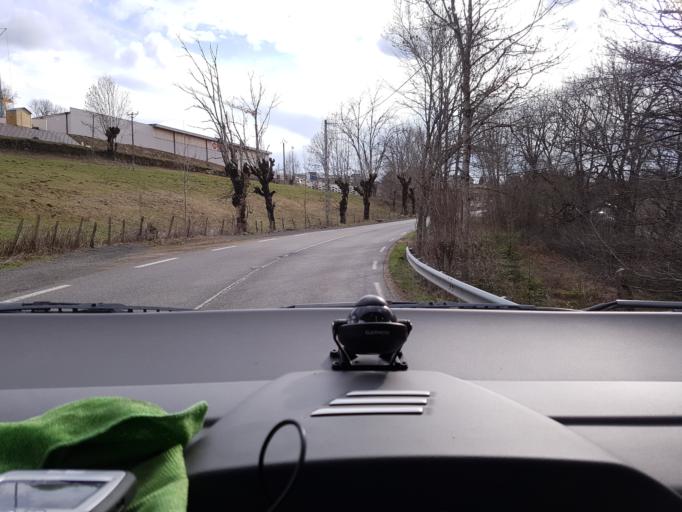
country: FR
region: Midi-Pyrenees
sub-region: Departement de l'Aveyron
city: Laguiole
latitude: 44.6874
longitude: 2.8539
